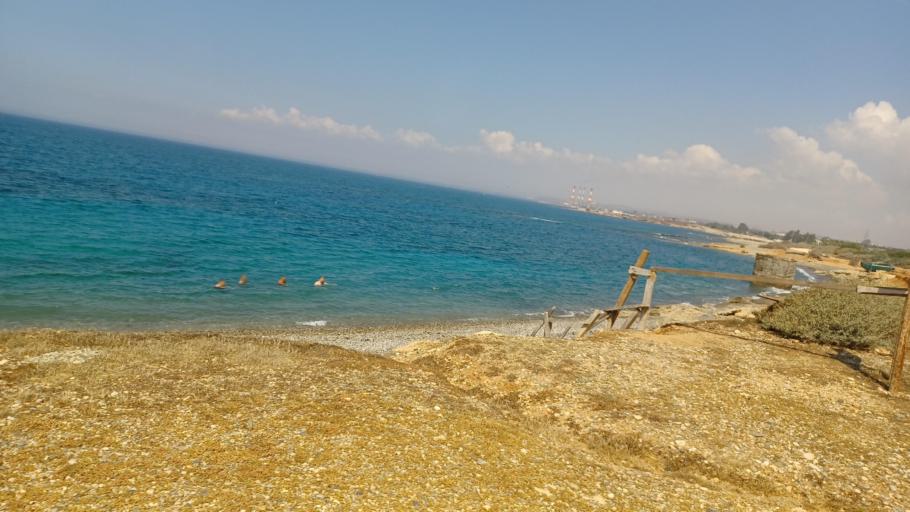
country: CY
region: Larnaka
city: Xylotymbou
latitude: 34.9784
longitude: 33.7829
